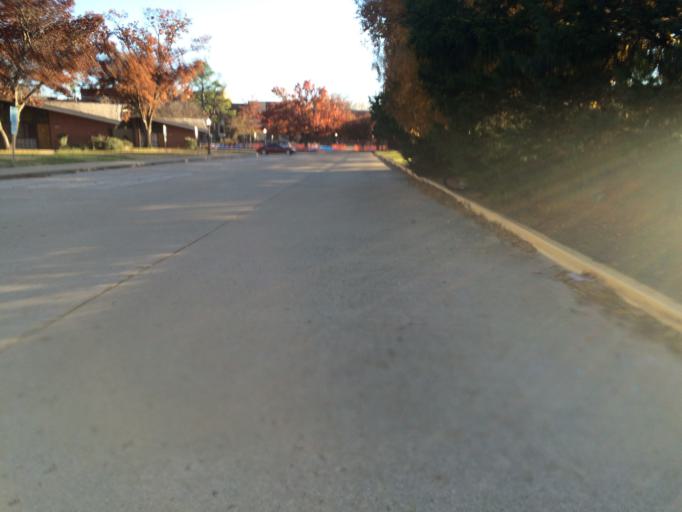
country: US
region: Oklahoma
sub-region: Cleveland County
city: Norman
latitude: 35.1979
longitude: -97.4472
